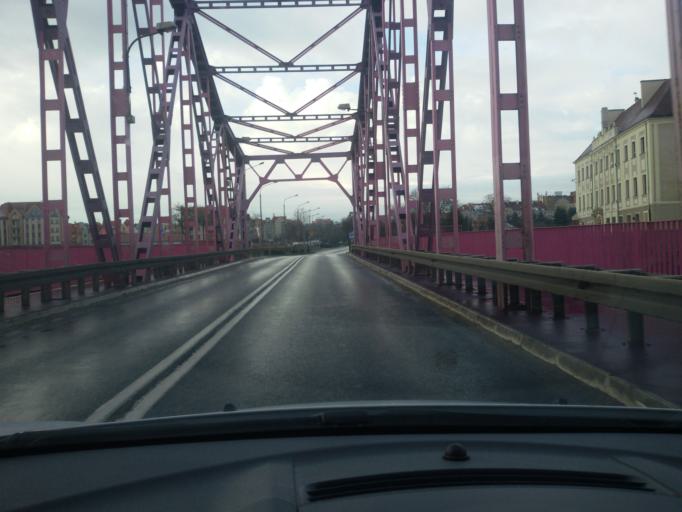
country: PL
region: Lower Silesian Voivodeship
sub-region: Powiat glogowski
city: Glogow
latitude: 51.6677
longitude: 16.0921
